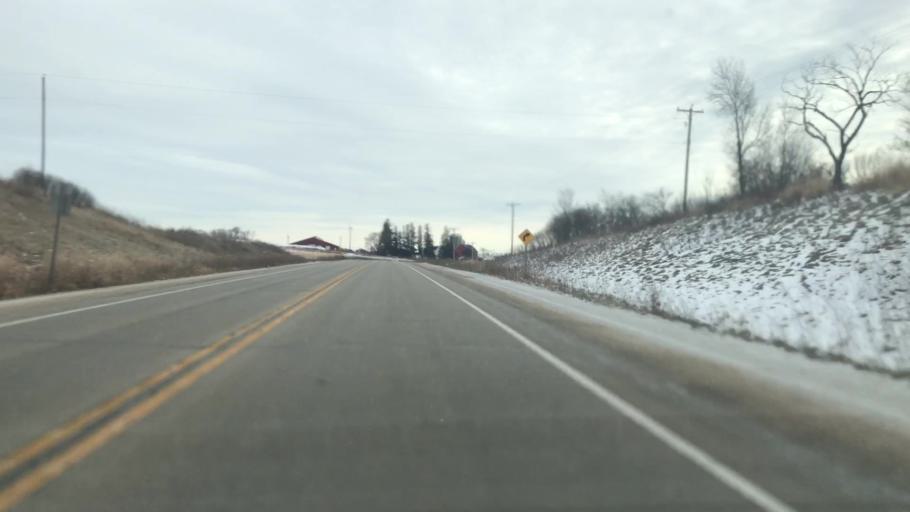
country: US
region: Wisconsin
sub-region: Dodge County
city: Mayville
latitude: 43.4428
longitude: -88.4966
